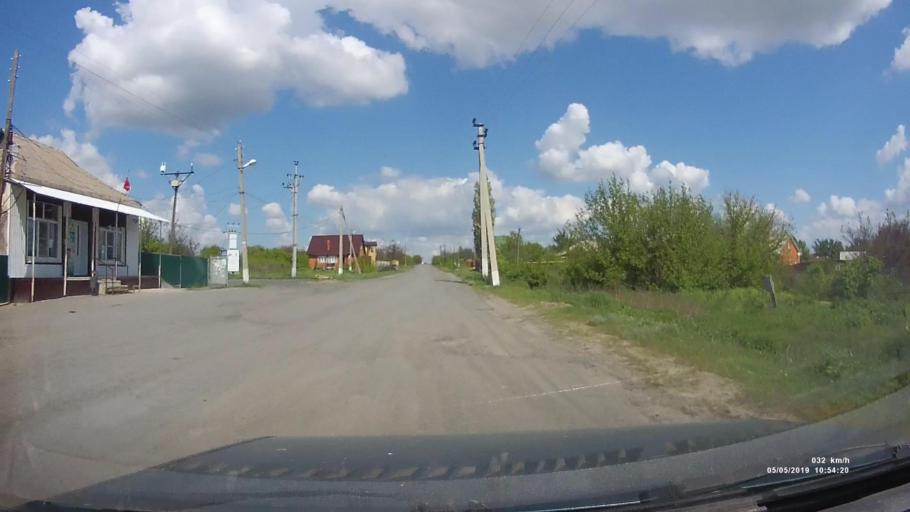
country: RU
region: Rostov
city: Ust'-Donetskiy
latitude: 47.6577
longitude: 40.8232
